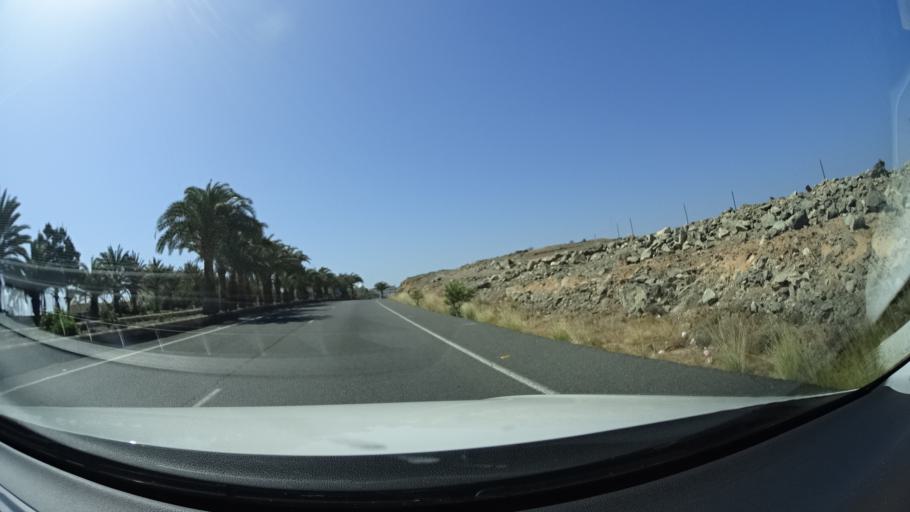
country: ES
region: Canary Islands
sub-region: Provincia de Las Palmas
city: Playa del Ingles
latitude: 27.7791
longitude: -15.5244
